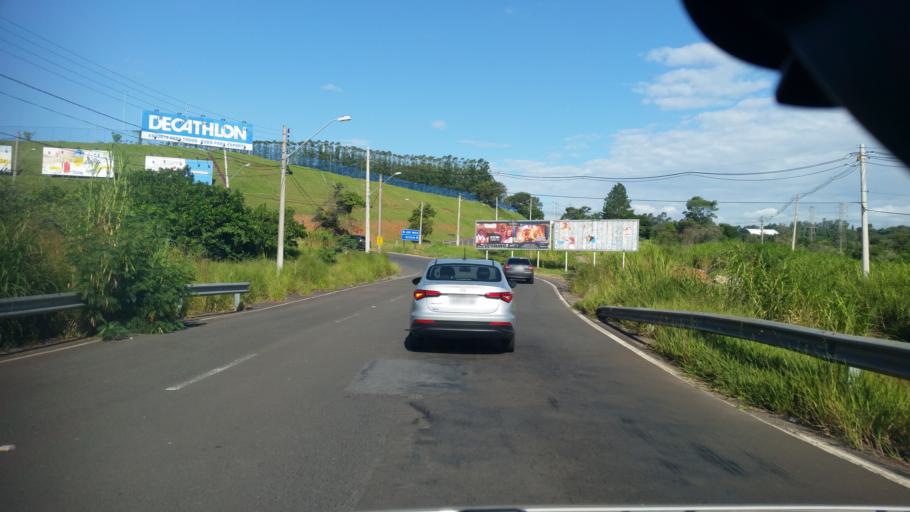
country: BR
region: Sao Paulo
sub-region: Campinas
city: Campinas
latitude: -22.8857
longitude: -47.0103
